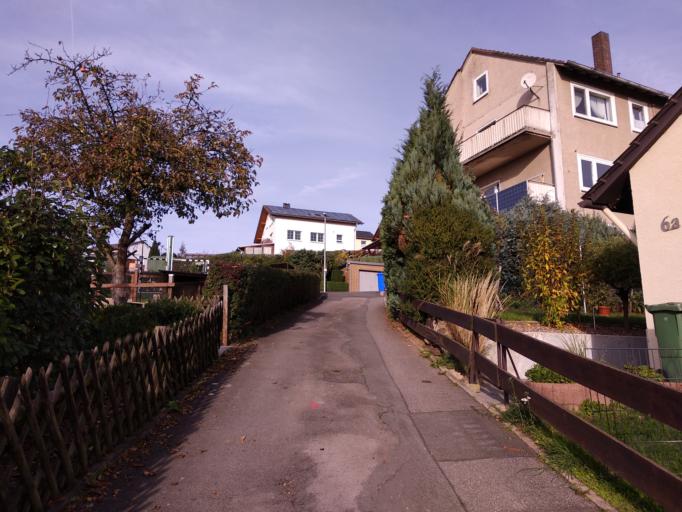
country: DE
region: North Rhine-Westphalia
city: Beverungen
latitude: 51.6740
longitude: 9.3707
